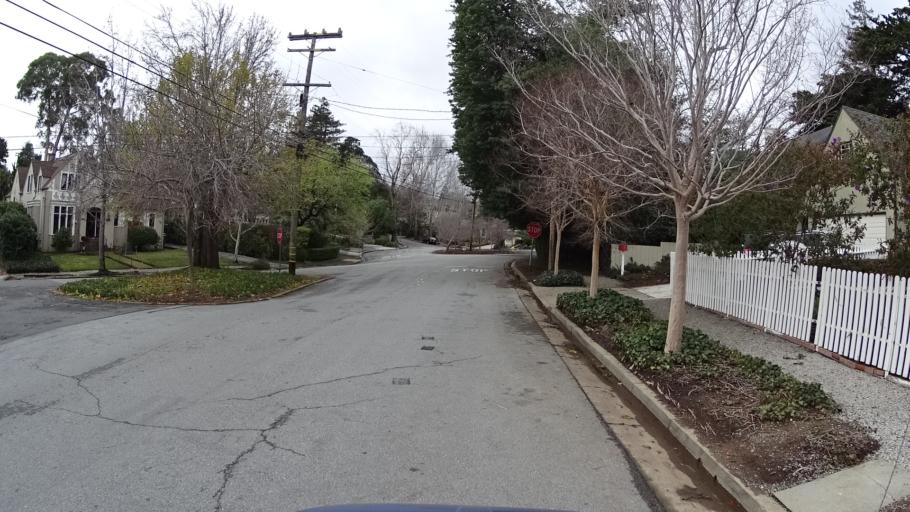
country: US
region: California
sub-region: San Mateo County
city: San Mateo
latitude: 37.5647
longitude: -122.3464
